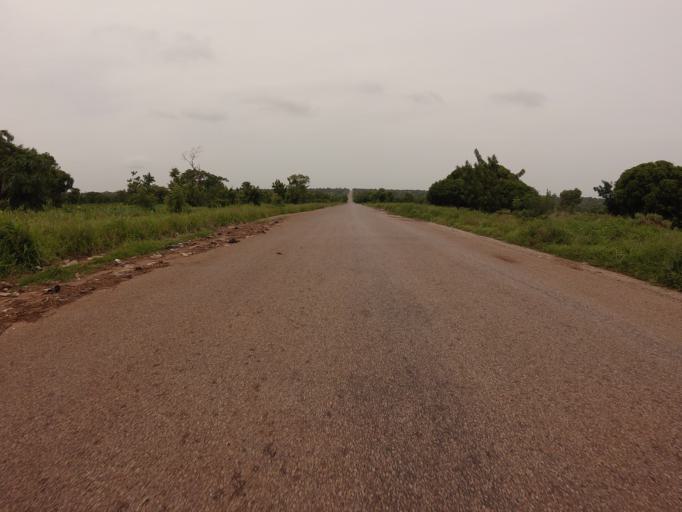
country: GH
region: Northern
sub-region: Yendi
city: Yendi
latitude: 9.3632
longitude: -0.0031
